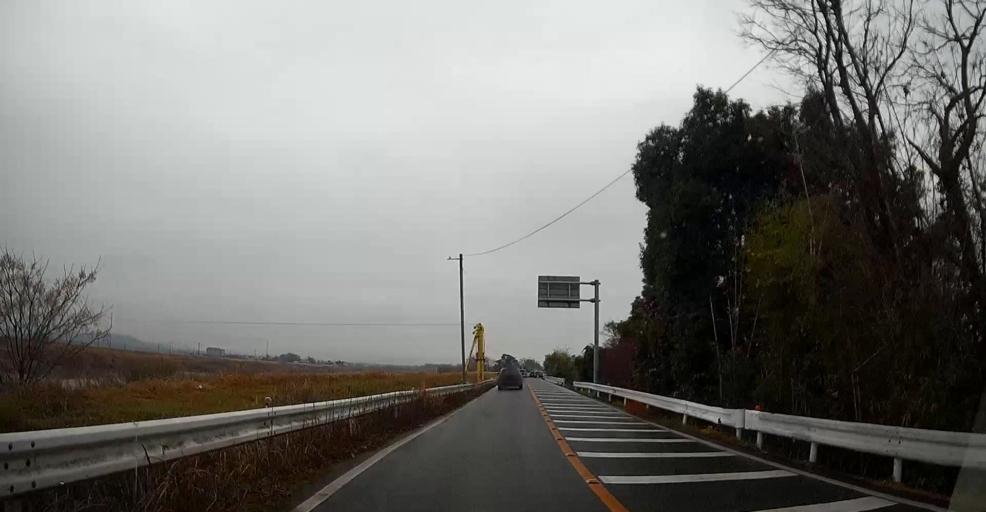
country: JP
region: Kumamoto
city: Kumamoto
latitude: 32.7598
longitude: 130.7527
